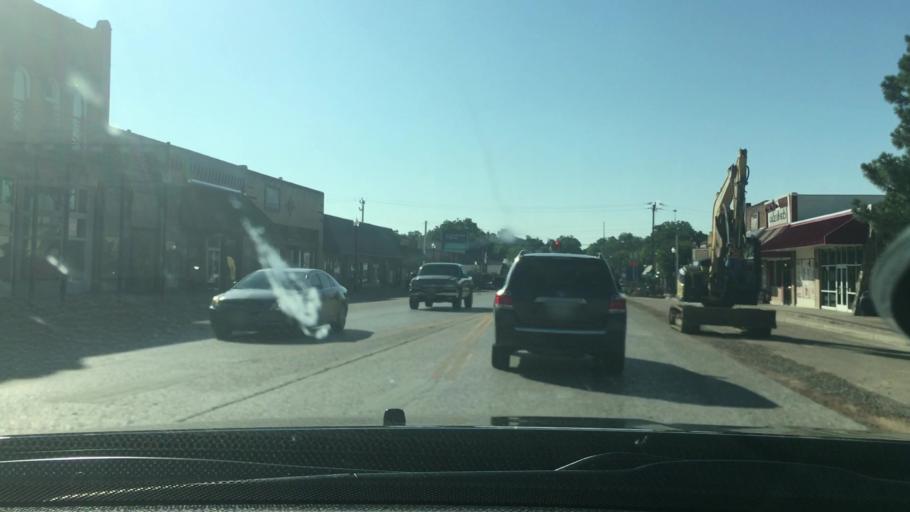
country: US
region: Oklahoma
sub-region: Johnston County
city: Tishomingo
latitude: 34.2359
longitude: -96.6794
